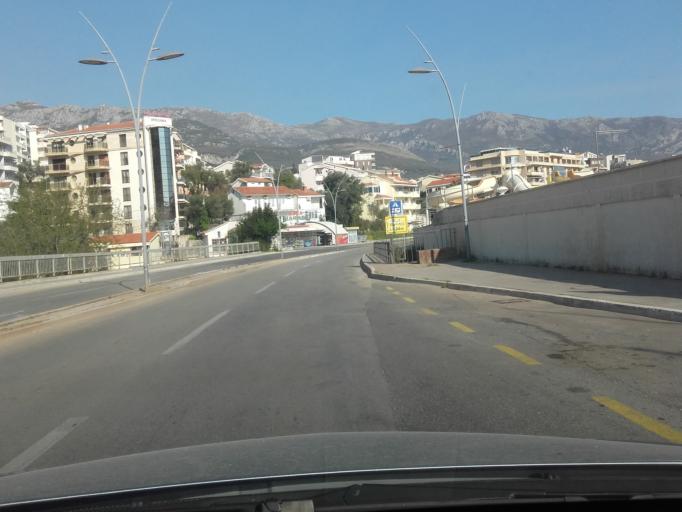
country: ME
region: Budva
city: Budva
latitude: 42.2836
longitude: 18.8637
